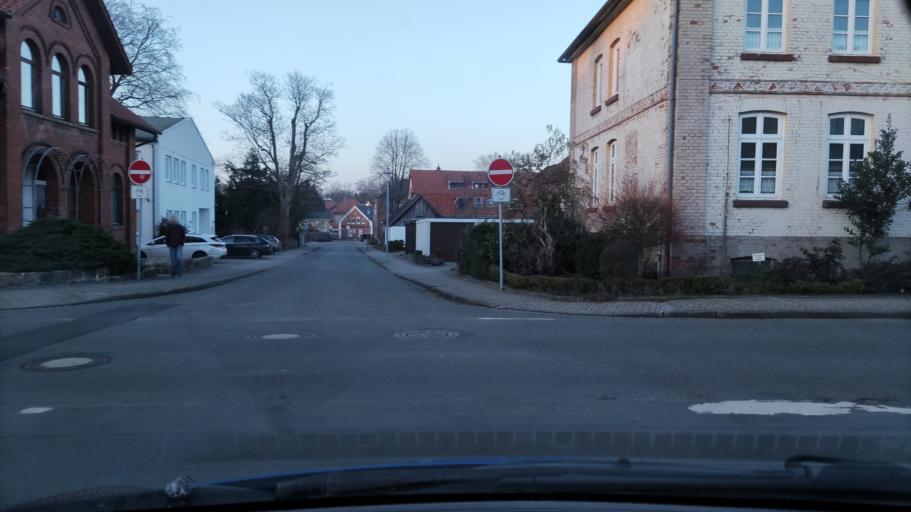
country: DE
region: Lower Saxony
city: Ebstorf
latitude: 53.0277
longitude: 10.4172
